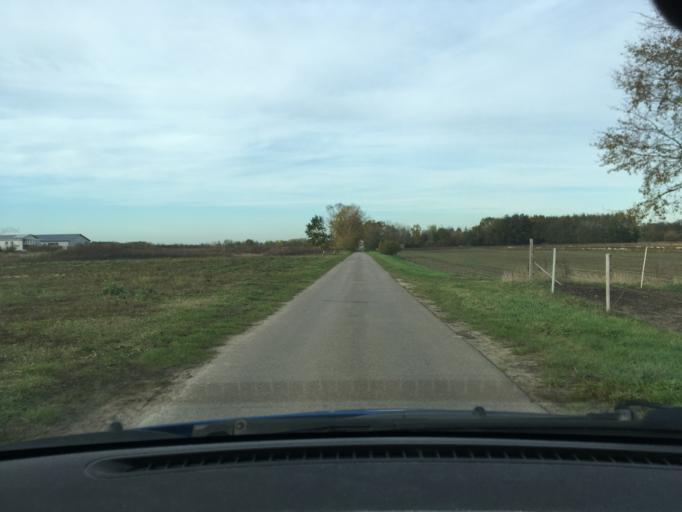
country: DE
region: Lower Saxony
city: Wittorf
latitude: 53.3139
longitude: 10.3768
